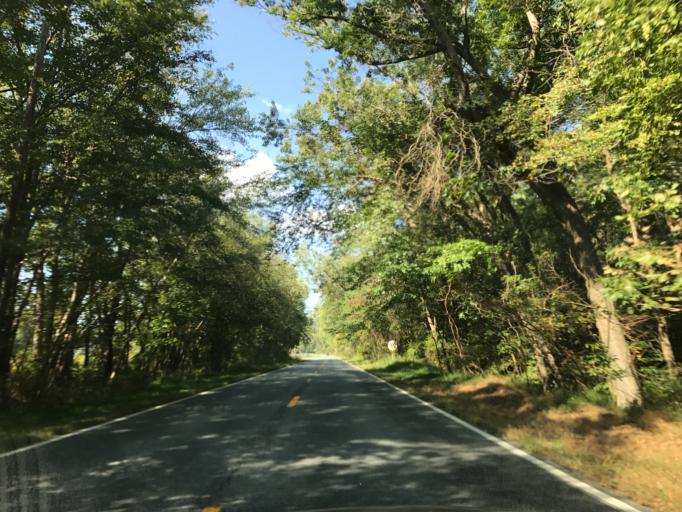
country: US
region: Maryland
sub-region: Cecil County
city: Rising Sun
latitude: 39.6537
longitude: -76.1538
